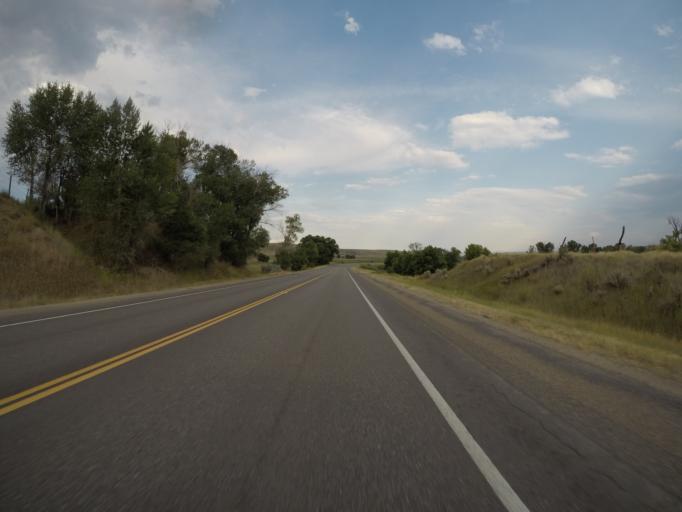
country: US
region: Colorado
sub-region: Moffat County
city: Craig
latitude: 40.5242
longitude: -107.4059
